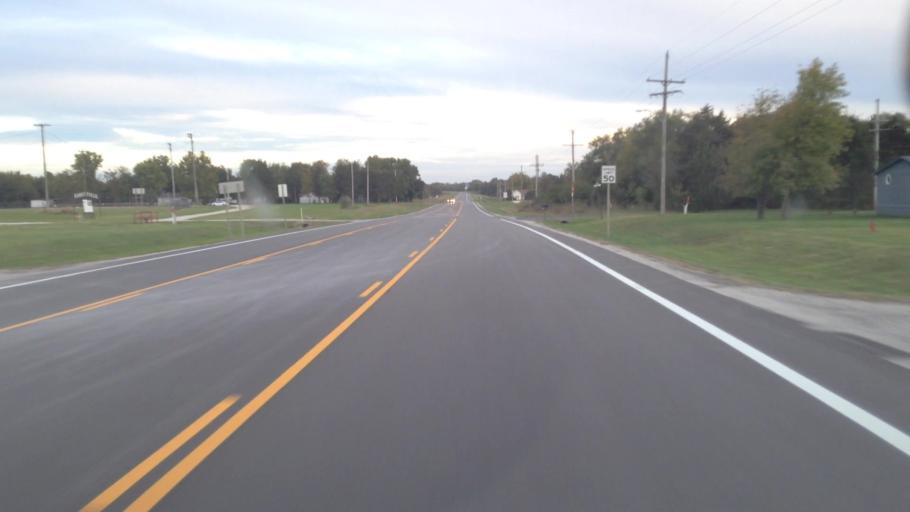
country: US
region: Kansas
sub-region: Franklin County
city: Ottawa
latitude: 38.4885
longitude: -95.2675
